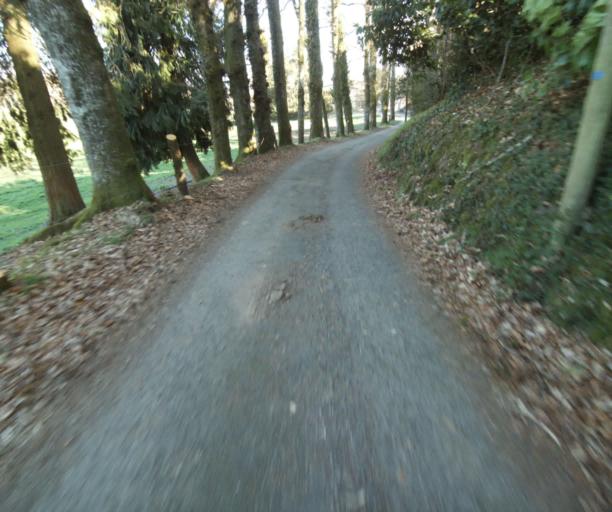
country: FR
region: Limousin
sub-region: Departement de la Correze
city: Seilhac
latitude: 45.3812
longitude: 1.7252
